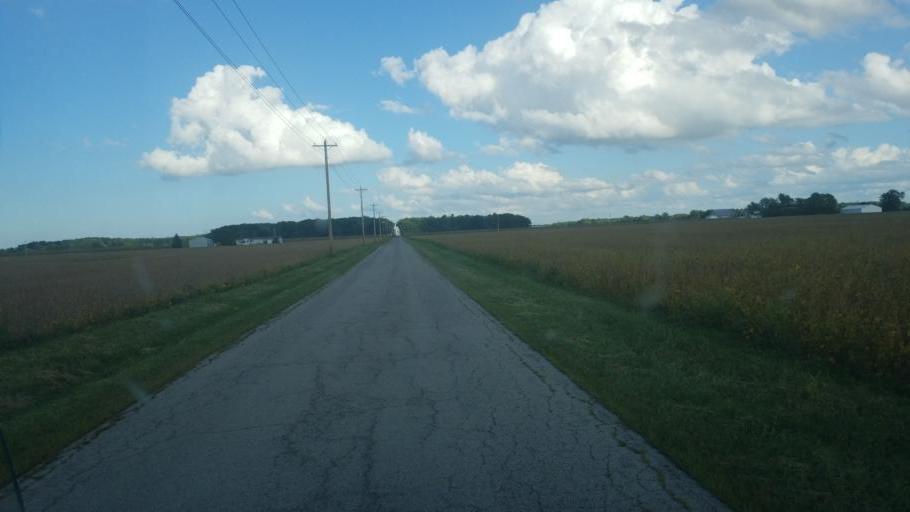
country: US
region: Ohio
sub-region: Hancock County
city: Arlington
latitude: 40.9363
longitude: -83.7334
